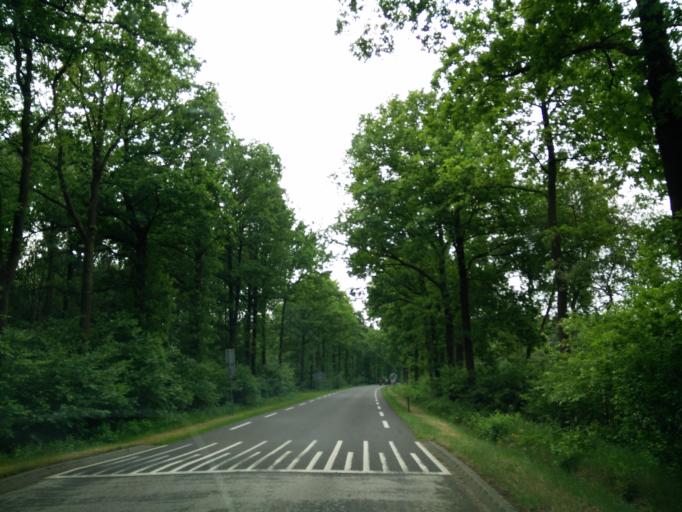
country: NL
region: Drenthe
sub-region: Gemeente Borger-Odoorn
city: Borger
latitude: 52.9453
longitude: 6.7139
